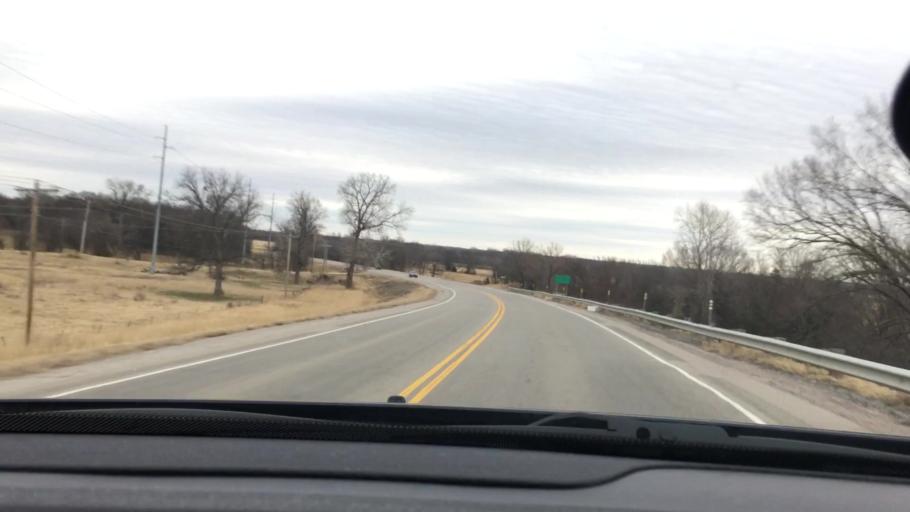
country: US
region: Oklahoma
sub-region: Marshall County
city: Oakland
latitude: 34.1880
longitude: -96.8052
